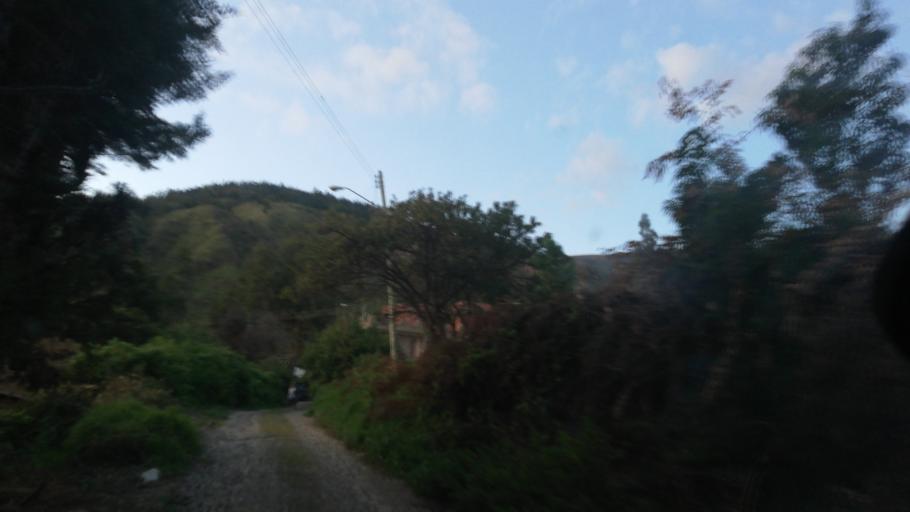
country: BO
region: Cochabamba
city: Cochabamba
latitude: -17.3186
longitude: -66.2085
